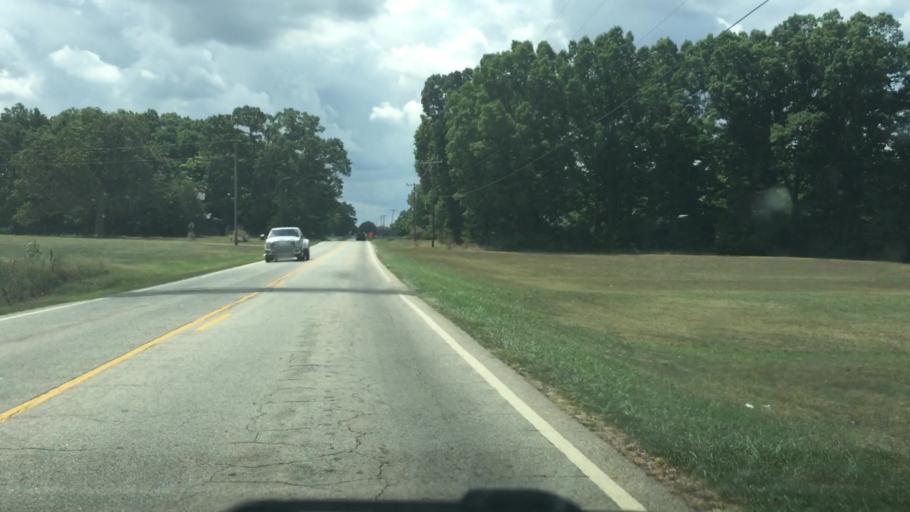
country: US
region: North Carolina
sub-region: Rowan County
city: Landis
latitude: 35.6116
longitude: -80.6537
